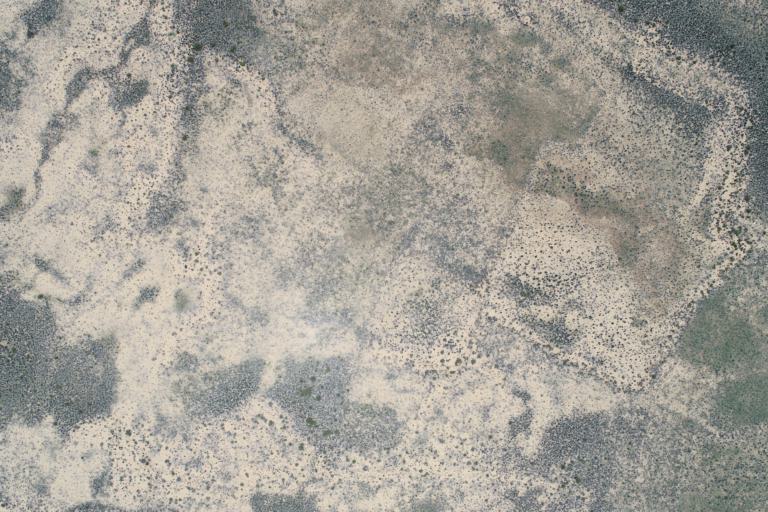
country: BO
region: La Paz
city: Curahuara de Carangas
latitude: -17.3078
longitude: -68.5115
